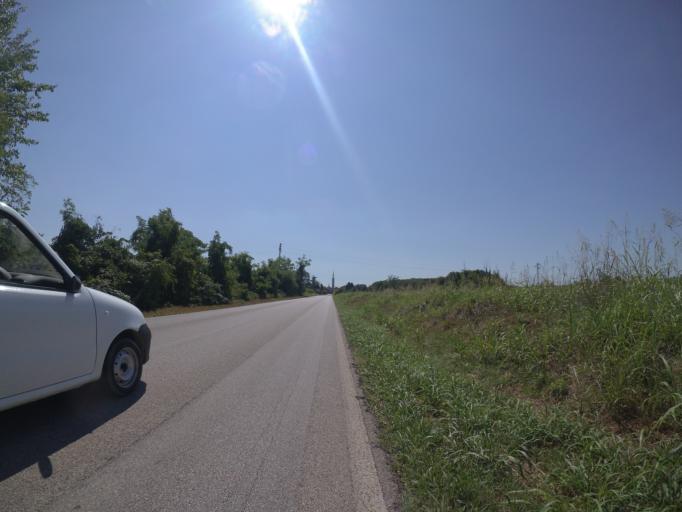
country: IT
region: Friuli Venezia Giulia
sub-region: Provincia di Udine
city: Mortegliano
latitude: 45.9560
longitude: 13.1686
